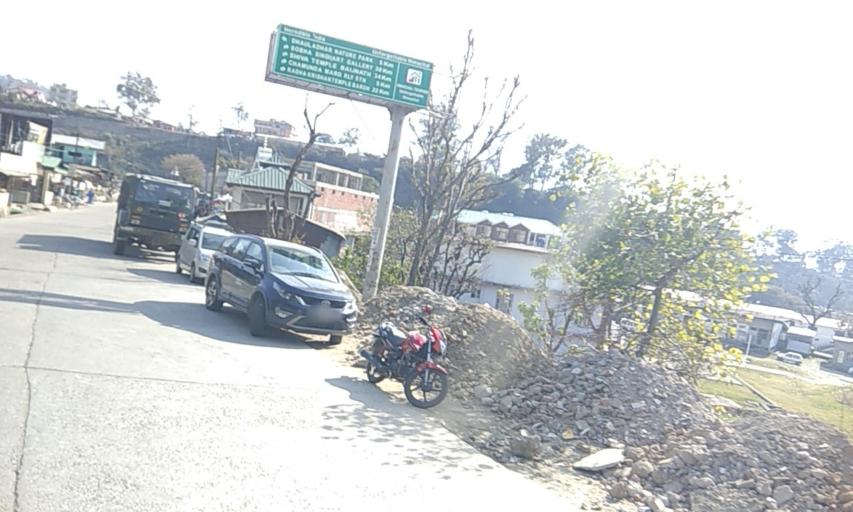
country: IN
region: Himachal Pradesh
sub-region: Kangra
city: Dharmsala
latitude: 32.1499
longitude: 76.4198
